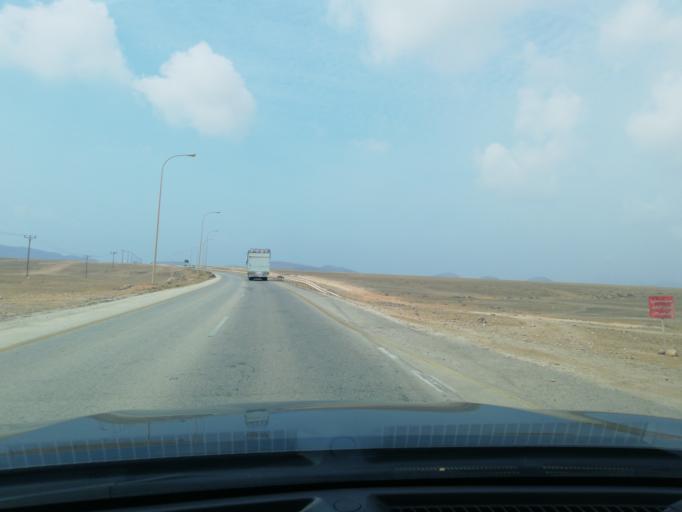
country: OM
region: Zufar
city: Salalah
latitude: 16.9379
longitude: 53.8441
